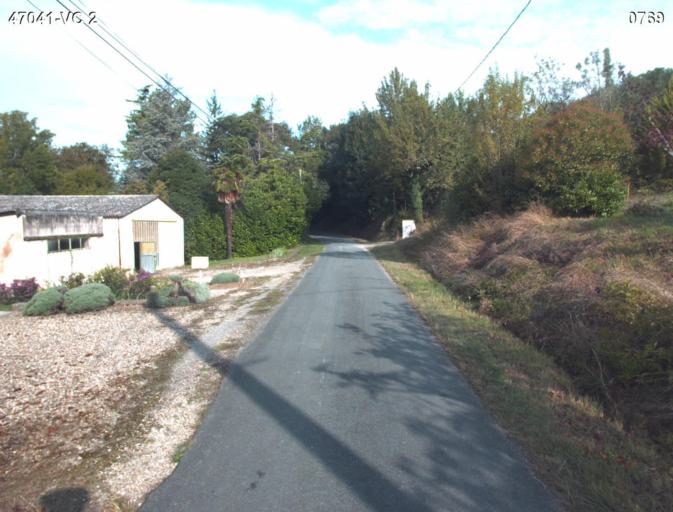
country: FR
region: Aquitaine
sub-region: Departement du Lot-et-Garonne
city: Port-Sainte-Marie
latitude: 44.1954
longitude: 0.4117
